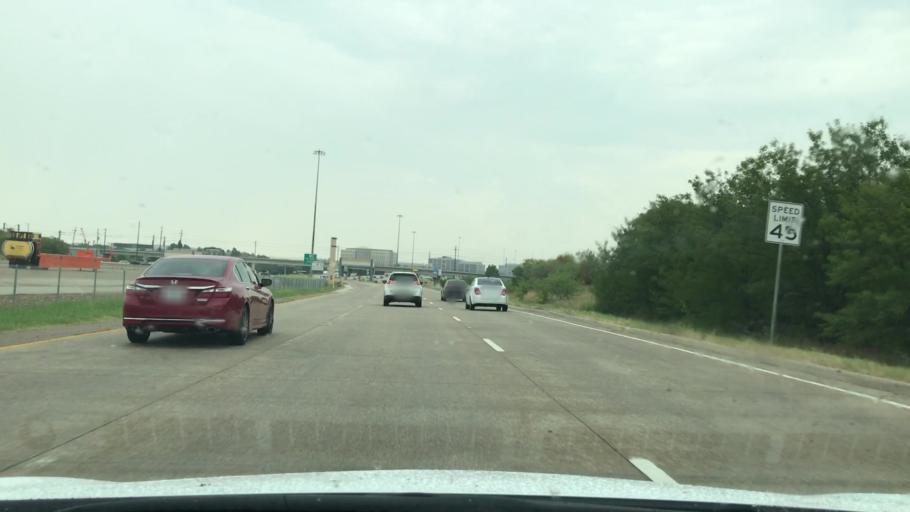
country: US
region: Texas
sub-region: Dallas County
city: Coppell
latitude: 32.8830
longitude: -96.9861
